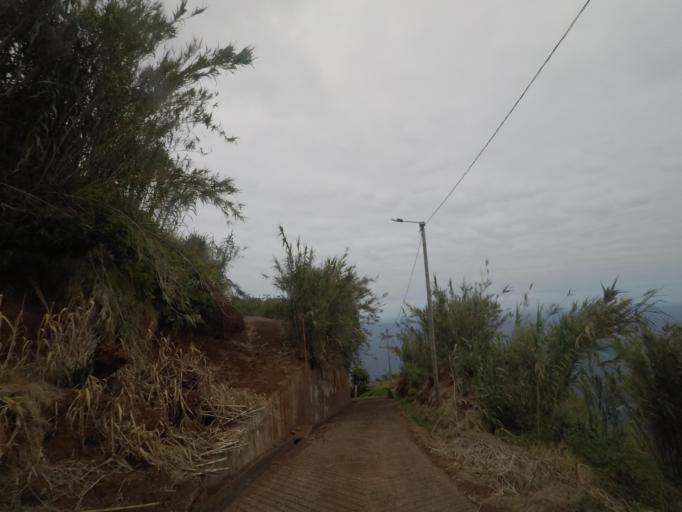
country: PT
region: Madeira
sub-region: Porto Moniz
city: Porto Moniz
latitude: 32.8626
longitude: -17.1804
